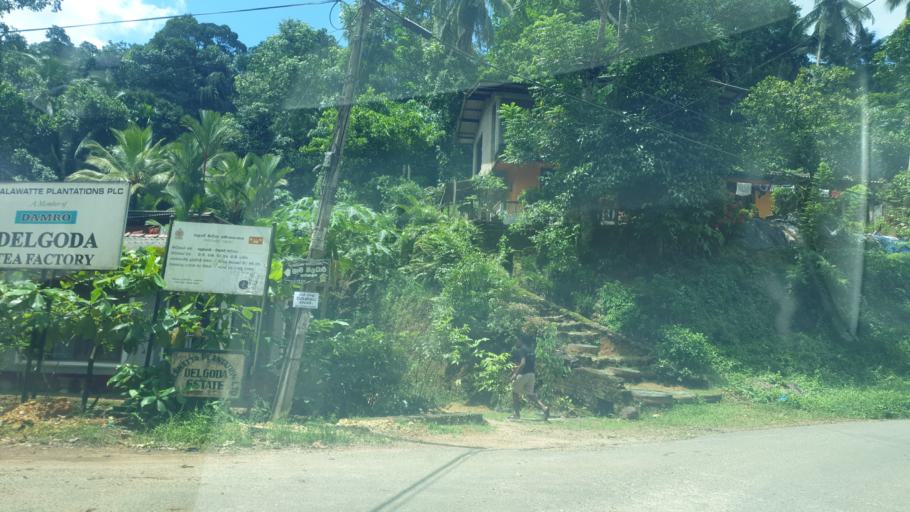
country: LK
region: Sabaragamuwa
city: Ratnapura
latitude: 6.4842
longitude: 80.4075
